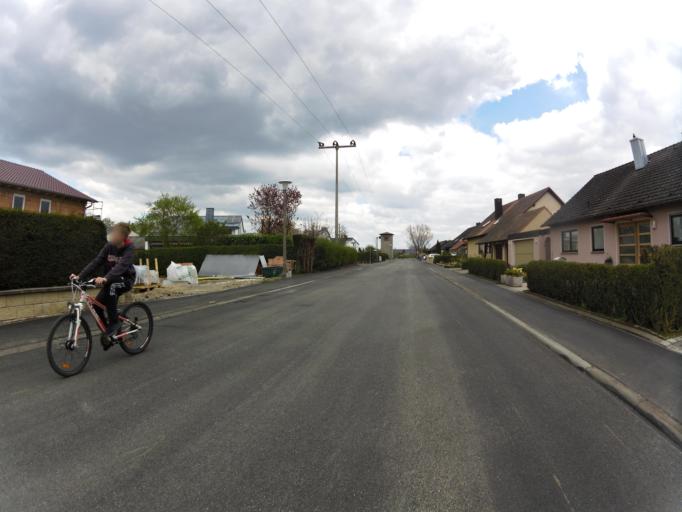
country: DE
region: Bavaria
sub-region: Regierungsbezirk Unterfranken
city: Giebelstadt
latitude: 49.6502
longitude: 9.9428
